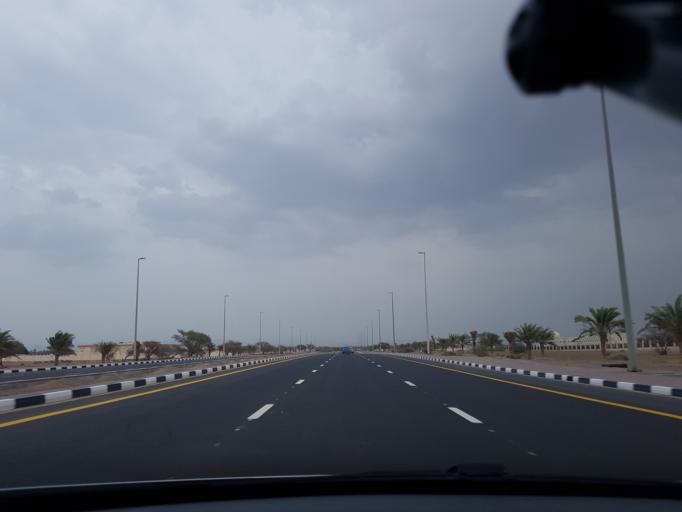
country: AE
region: Ash Shariqah
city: Adh Dhayd
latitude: 25.2675
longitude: 55.9059
